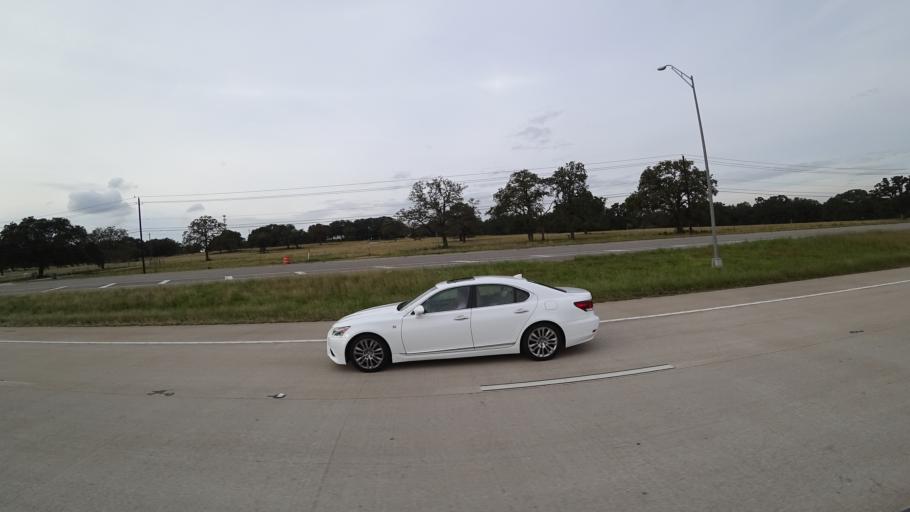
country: US
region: Texas
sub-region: Williamson County
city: Brushy Creek
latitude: 30.4800
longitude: -97.7545
